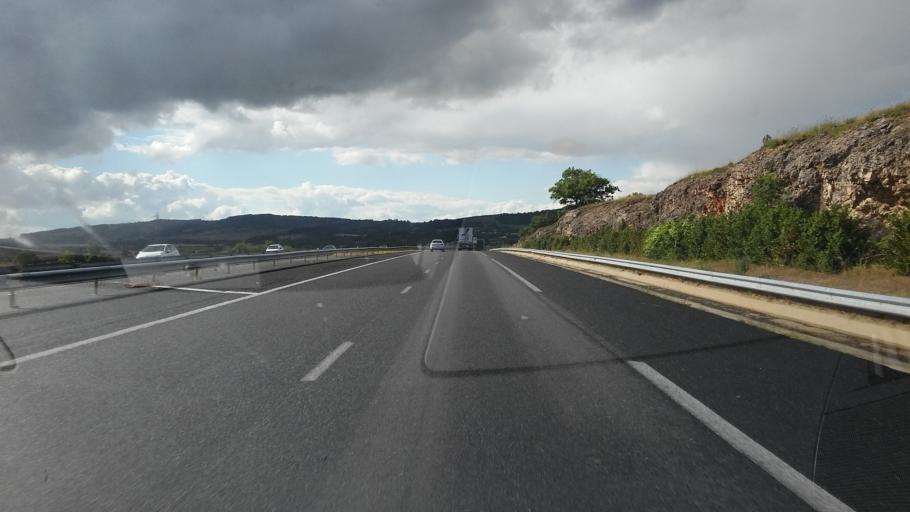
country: FR
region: Midi-Pyrenees
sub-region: Departement de l'Aveyron
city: La Cavalerie
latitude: 43.9453
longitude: 3.2215
